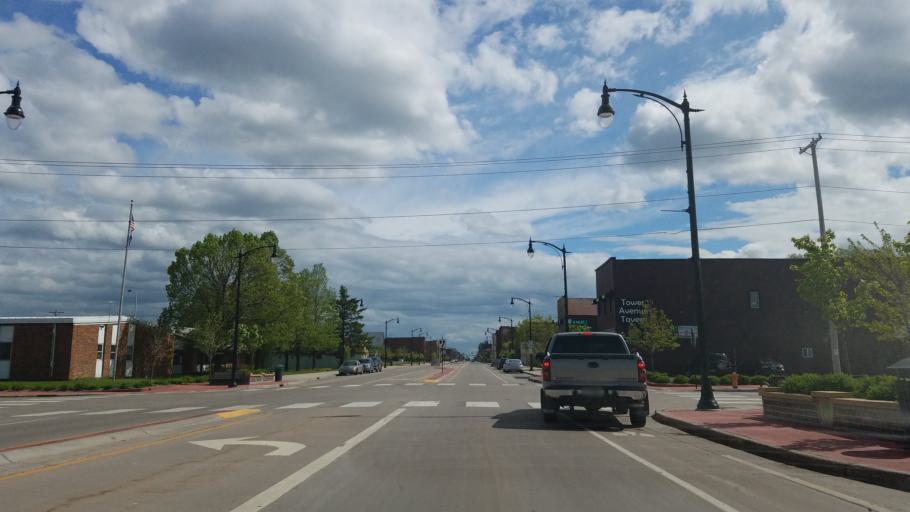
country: US
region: Wisconsin
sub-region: Douglas County
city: Superior
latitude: 46.7344
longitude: -92.1039
